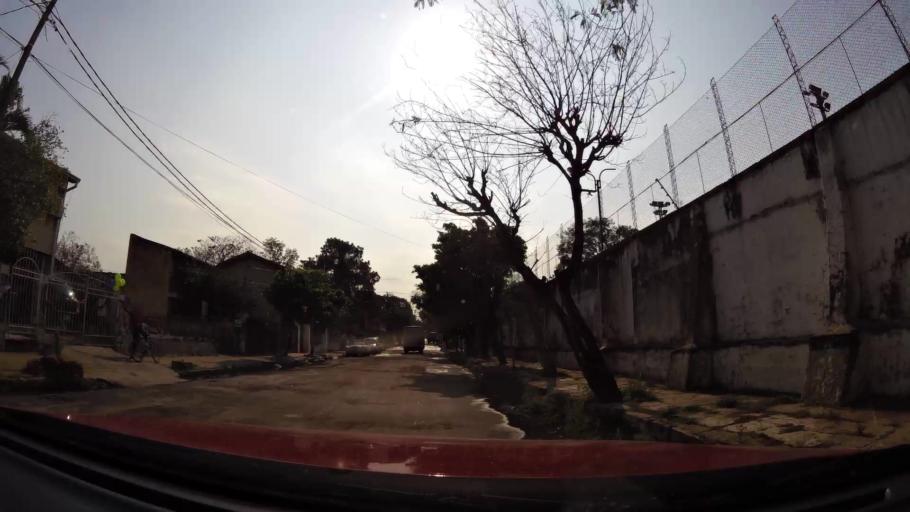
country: PY
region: Presidente Hayes
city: Nanawa
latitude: -25.2941
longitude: -57.6690
